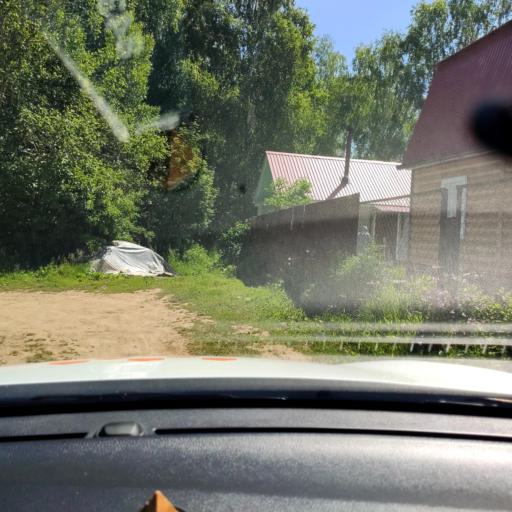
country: RU
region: Tatarstan
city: Vysokaya Gora
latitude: 55.8121
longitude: 49.2881
